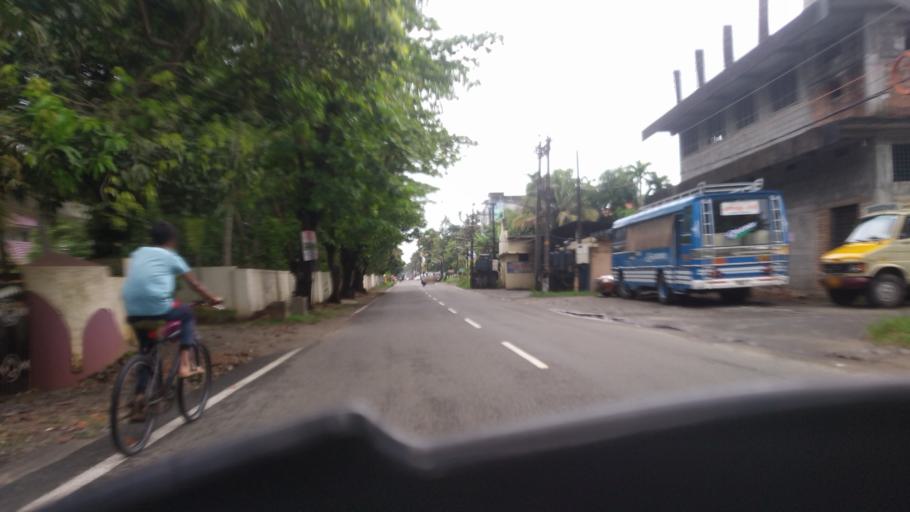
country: IN
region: Kerala
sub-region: Ernakulam
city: Elur
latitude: 10.0964
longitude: 76.2062
